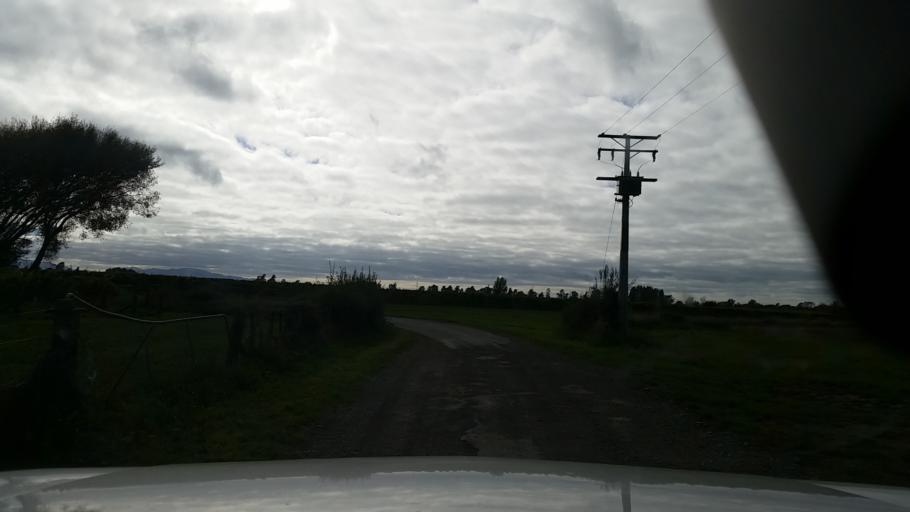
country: NZ
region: Marlborough
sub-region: Marlborough District
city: Blenheim
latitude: -41.4615
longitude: 173.9987
